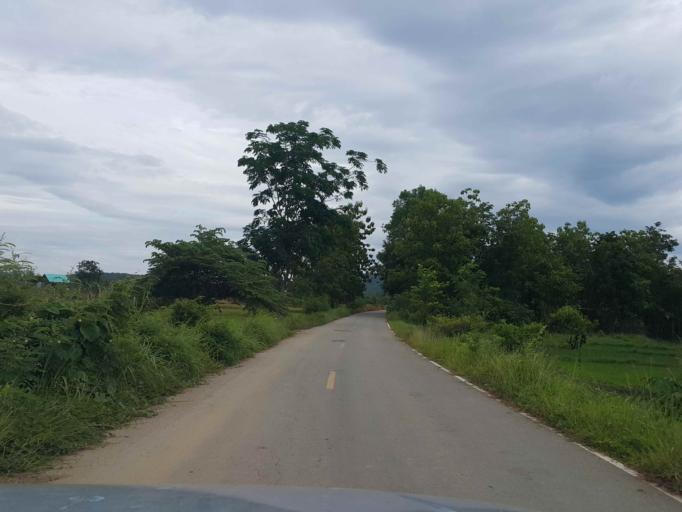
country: TH
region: Sukhothai
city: Thung Saliam
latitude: 17.3334
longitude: 99.4397
